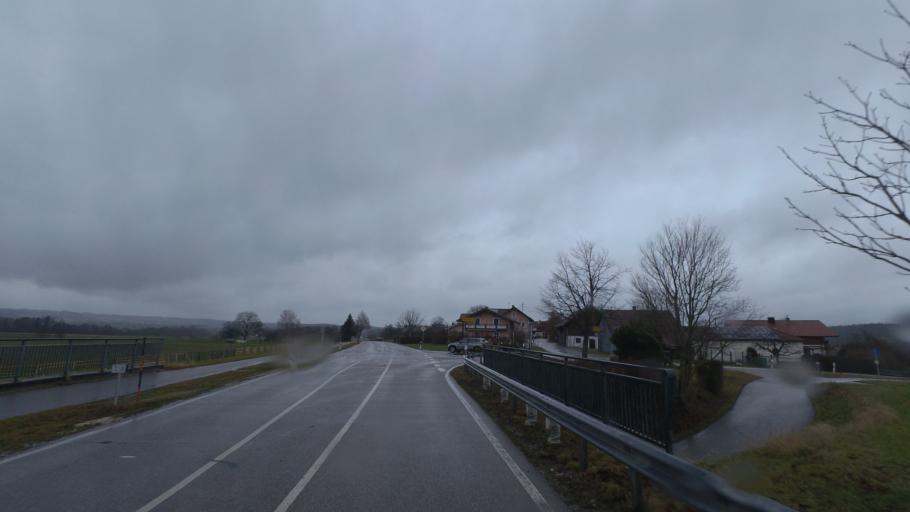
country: DE
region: Bavaria
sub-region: Upper Bavaria
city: Petting
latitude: 47.9405
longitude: 12.8020
